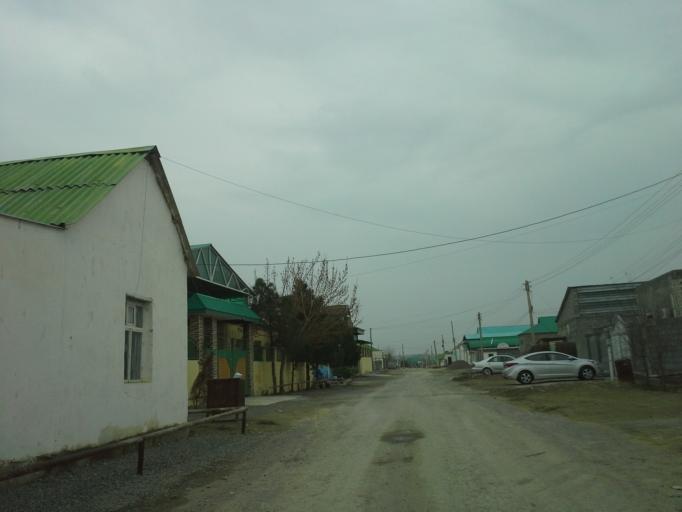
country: TM
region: Ahal
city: Abadan
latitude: 37.9706
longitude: 58.2289
